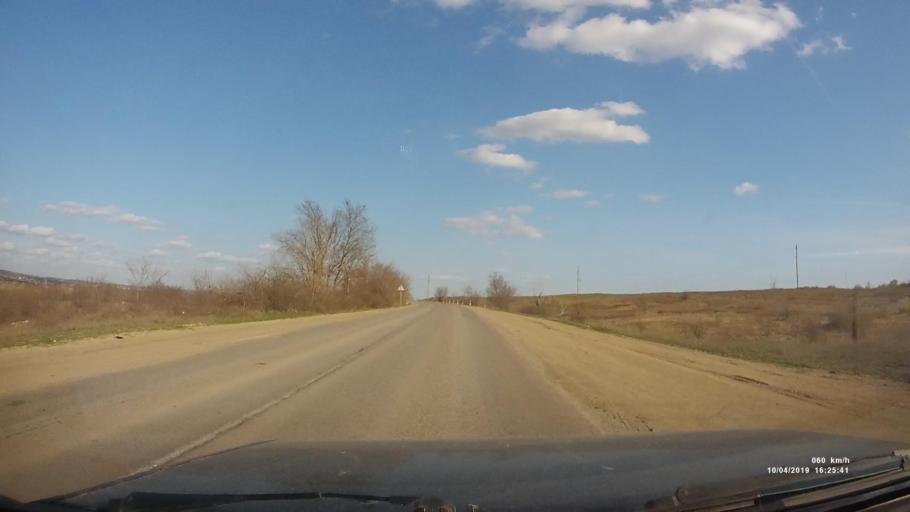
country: RU
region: Rostov
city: Staraya Stanitsa
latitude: 48.2915
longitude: 40.3261
